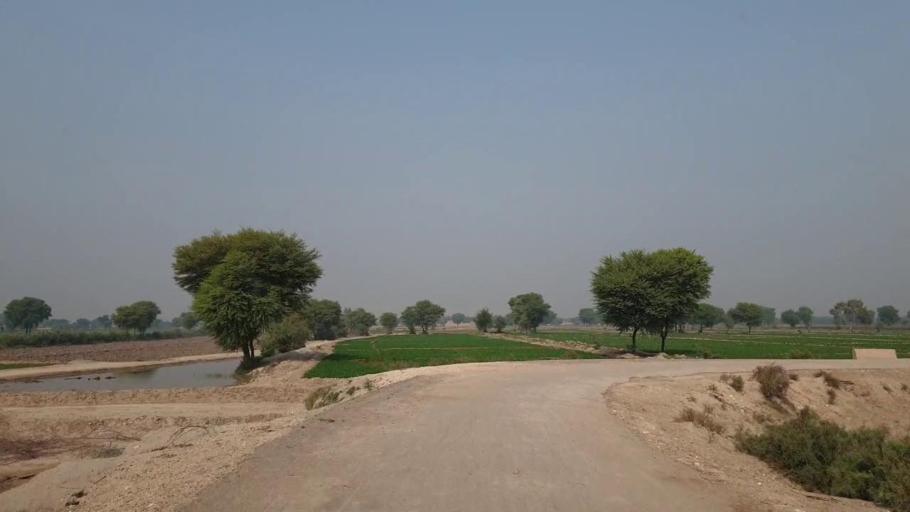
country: PK
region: Sindh
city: Bhan
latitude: 26.5183
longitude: 67.7284
